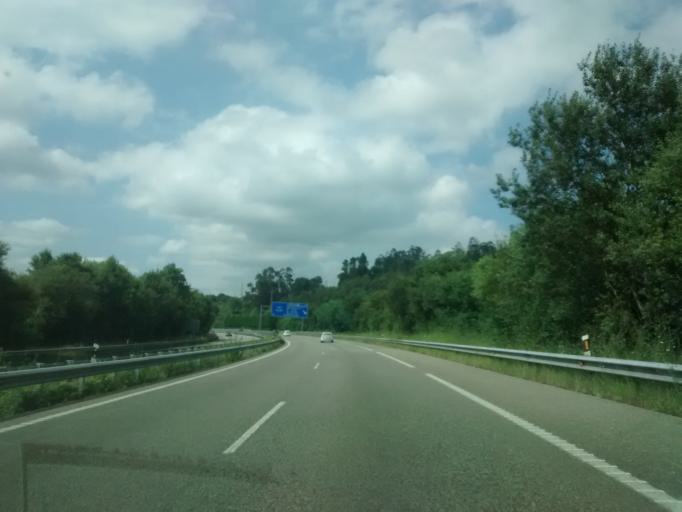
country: ES
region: Asturias
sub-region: Province of Asturias
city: Pola de Siero
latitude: 43.3690
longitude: -5.6817
